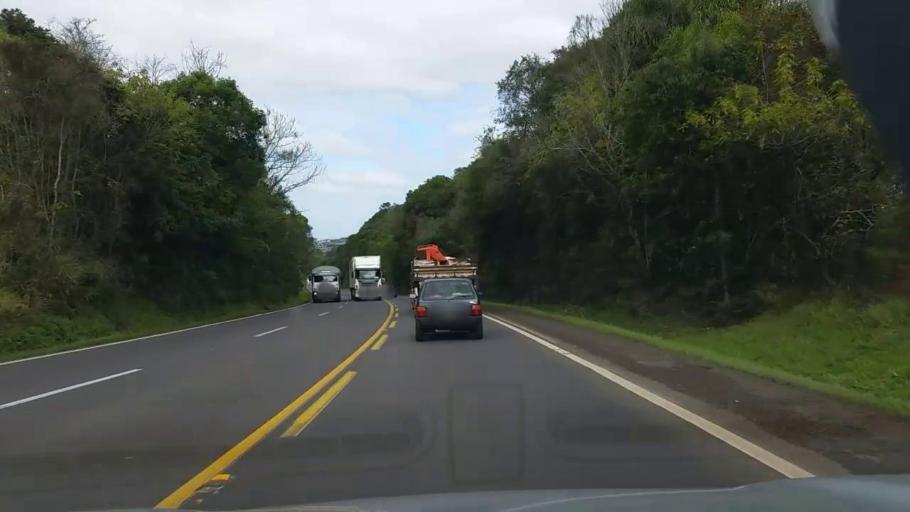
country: BR
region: Rio Grande do Sul
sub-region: Arroio Do Meio
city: Arroio do Meio
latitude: -29.3949
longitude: -52.0426
